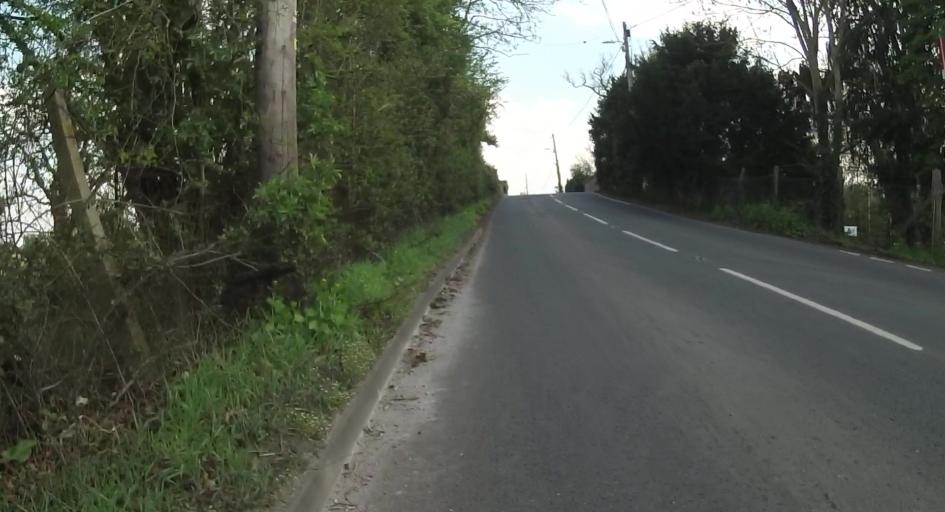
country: GB
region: England
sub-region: West Berkshire
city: Stratfield Mortimer
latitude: 51.3728
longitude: -1.0353
